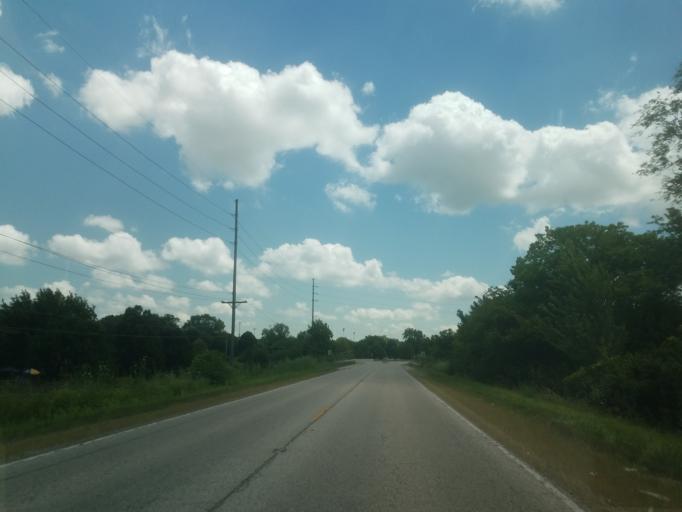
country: US
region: Illinois
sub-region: McLean County
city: Bloomington
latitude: 40.4901
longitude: -89.0170
